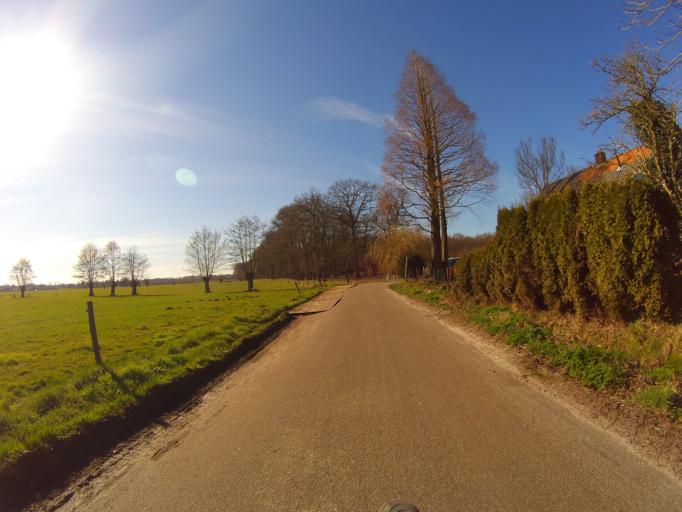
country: NL
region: Utrecht
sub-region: Gemeente Utrechtse Heuvelrug
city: Overberg
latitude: 52.0573
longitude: 5.4919
